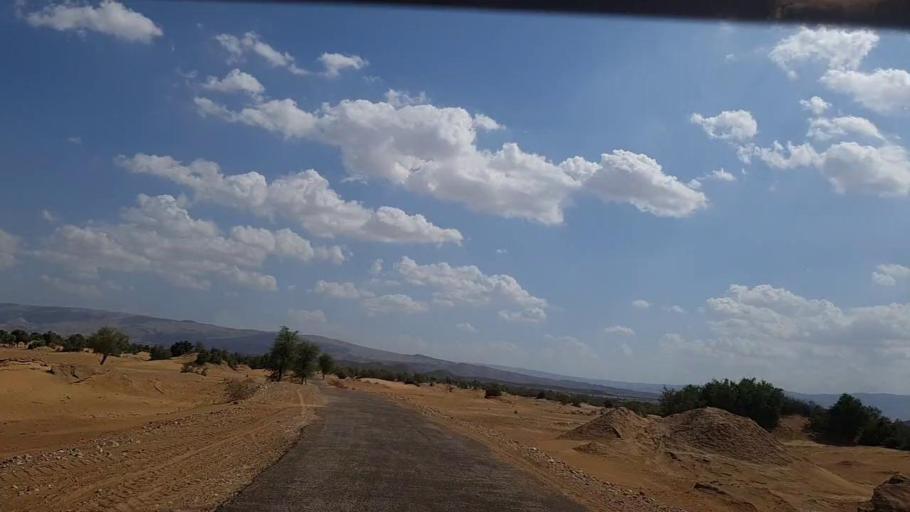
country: PK
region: Sindh
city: Johi
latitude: 26.5148
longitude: 67.4490
